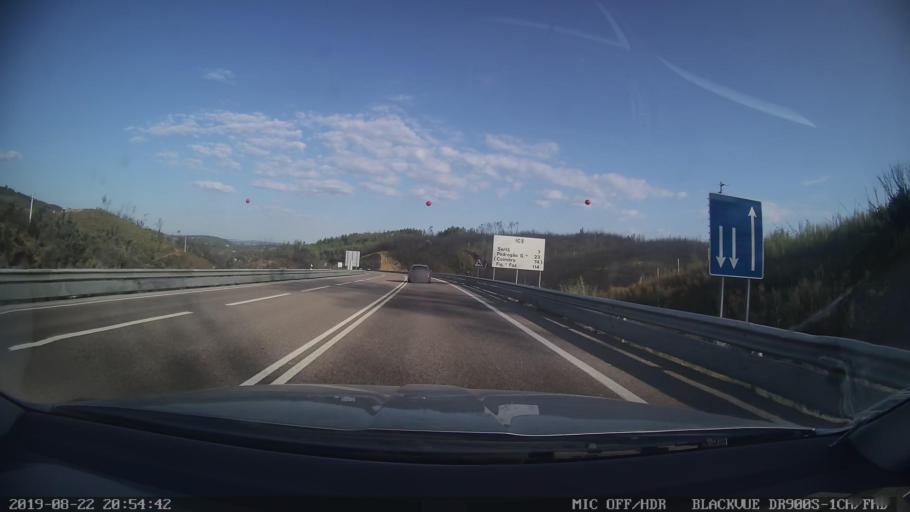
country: PT
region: Castelo Branco
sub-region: Serta
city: Serta
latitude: 39.7759
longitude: -8.0182
